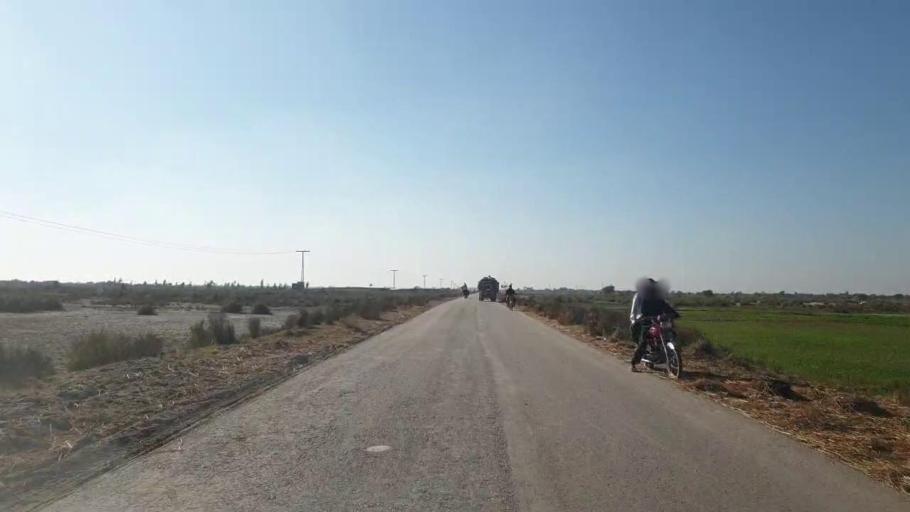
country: PK
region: Sindh
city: New Badah
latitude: 27.3249
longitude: 68.0589
